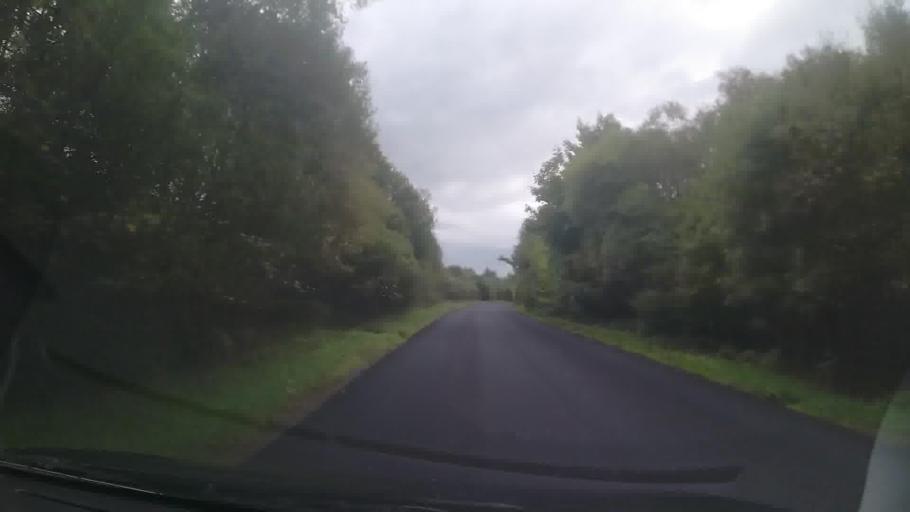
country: GB
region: Scotland
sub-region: Argyll and Bute
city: Garelochhead
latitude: 56.2372
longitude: -4.9630
